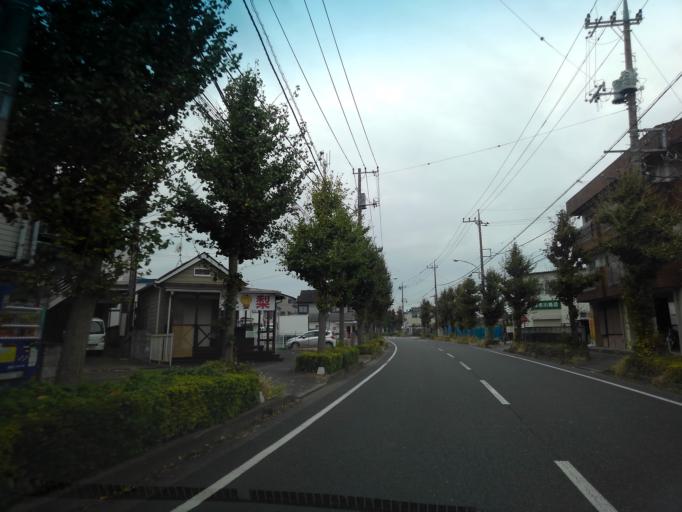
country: JP
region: Tokyo
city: Chofugaoka
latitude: 35.6450
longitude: 139.5170
